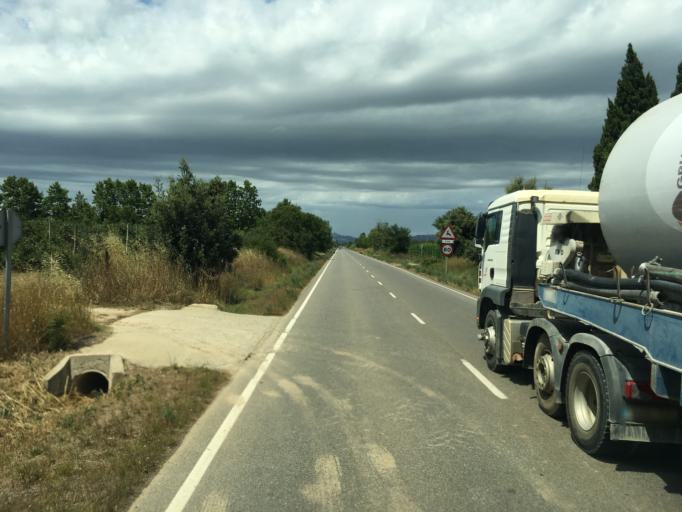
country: ES
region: Catalonia
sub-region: Provincia de Girona
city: Sant Pere Pescador
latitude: 42.1971
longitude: 3.0832
